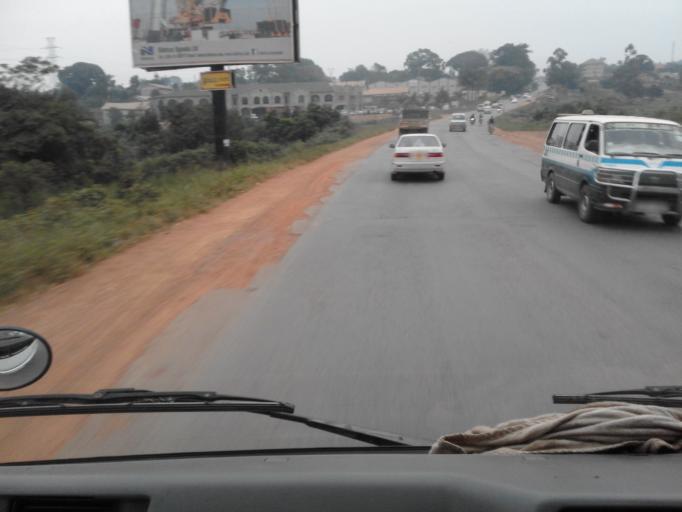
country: UG
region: Central Region
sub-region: Wakiso District
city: Bweyogerere
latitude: 0.3664
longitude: 32.7043
